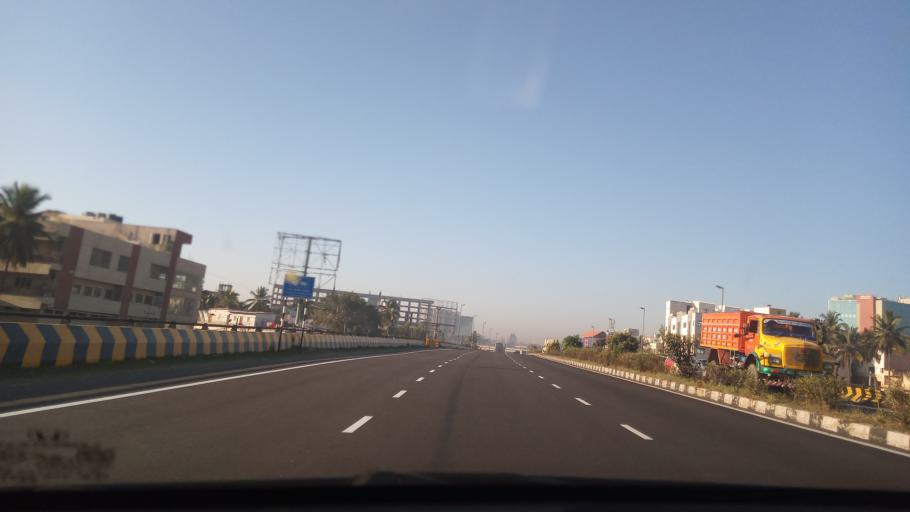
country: IN
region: Karnataka
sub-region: Bangalore Urban
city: Yelahanka
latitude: 13.0987
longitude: 77.5992
